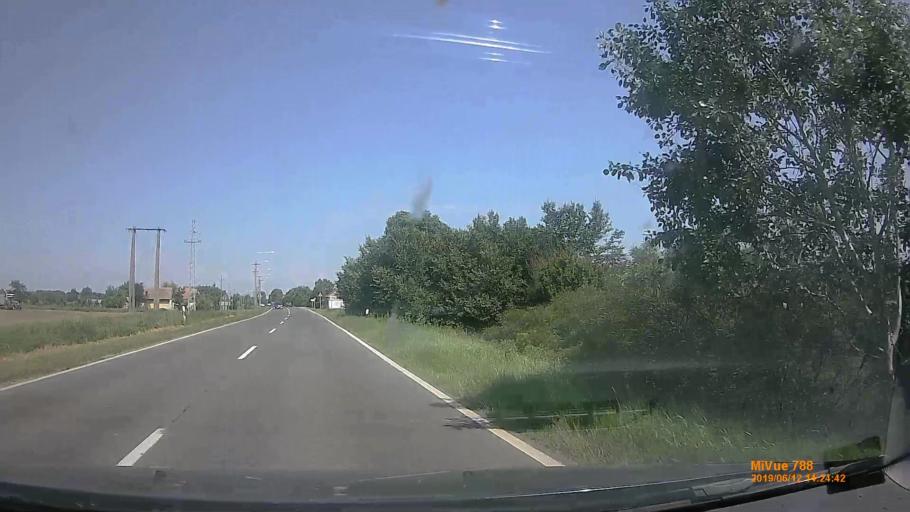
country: HU
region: Csongrad
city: Maroslele
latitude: 46.2184
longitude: 20.3165
